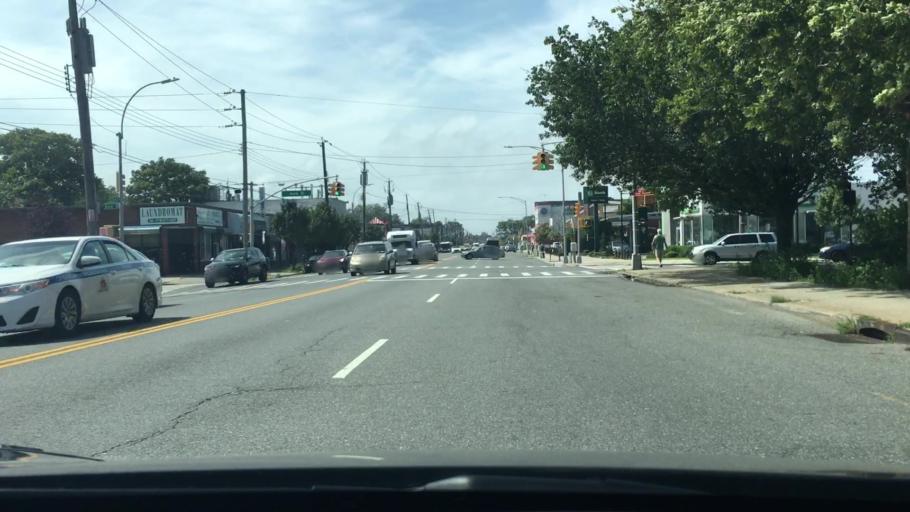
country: US
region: New York
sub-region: Kings County
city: Brooklyn
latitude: 40.6161
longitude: -73.9295
